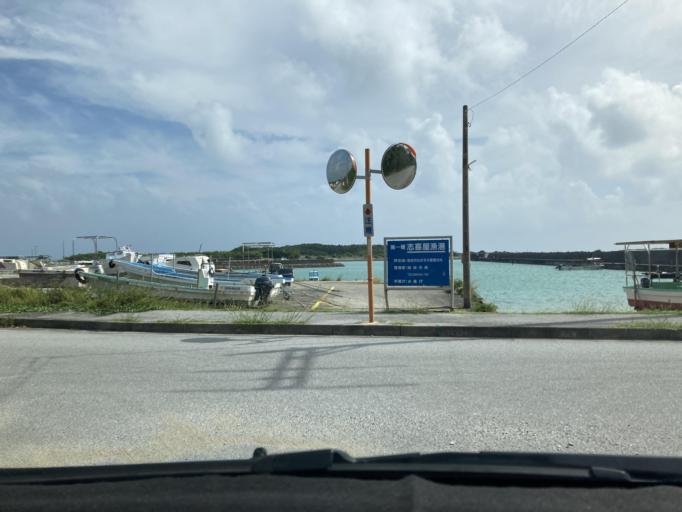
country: JP
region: Okinawa
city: Ginowan
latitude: 26.1492
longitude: 127.8053
